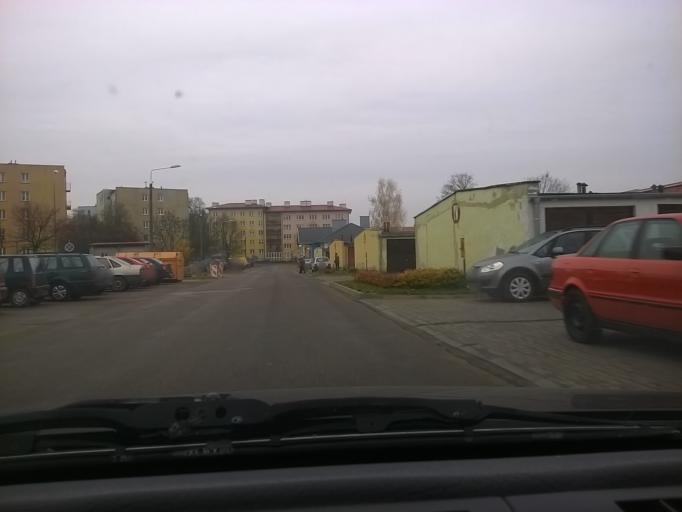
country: PL
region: Warmian-Masurian Voivodeship
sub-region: Powiat ketrzynski
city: Ketrzyn
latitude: 54.0824
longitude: 21.3621
